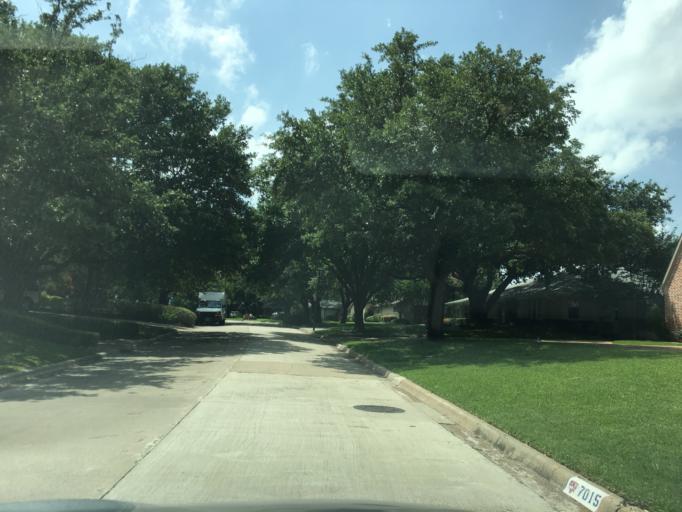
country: US
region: Texas
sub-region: Dallas County
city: University Park
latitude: 32.8753
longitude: -96.7836
